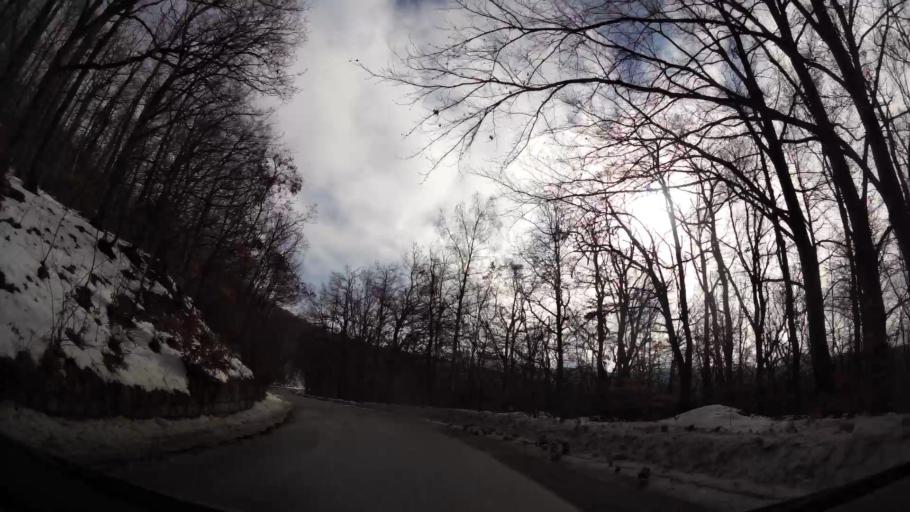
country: BG
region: Sofia-Capital
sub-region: Stolichna Obshtina
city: Sofia
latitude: 42.6342
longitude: 23.2259
